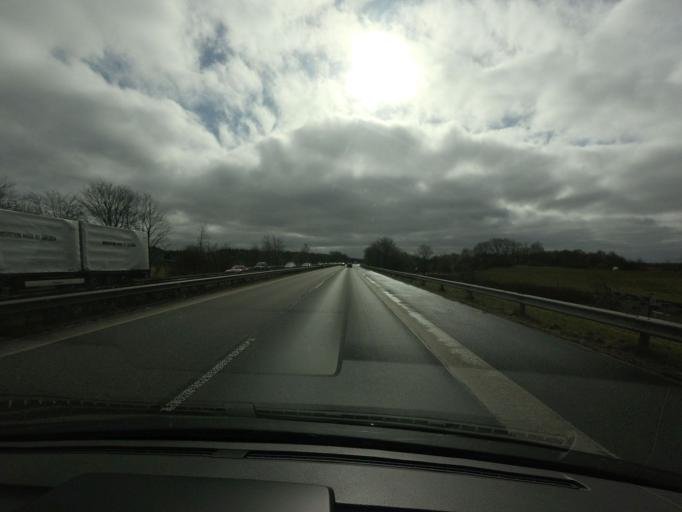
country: DE
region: Schleswig-Holstein
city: Alt Duvenstedt
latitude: 54.3921
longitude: 9.6500
